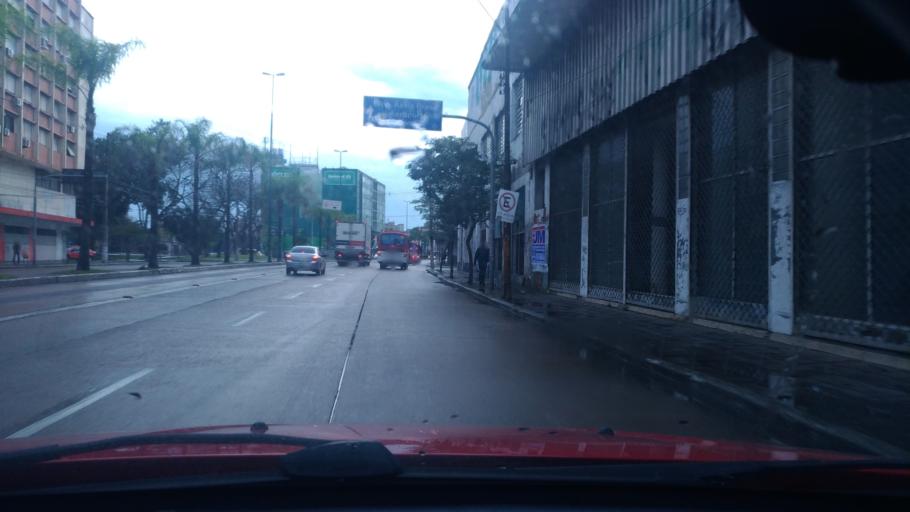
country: BR
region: Rio Grande do Sul
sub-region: Porto Alegre
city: Porto Alegre
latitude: -30.0185
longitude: -51.2093
